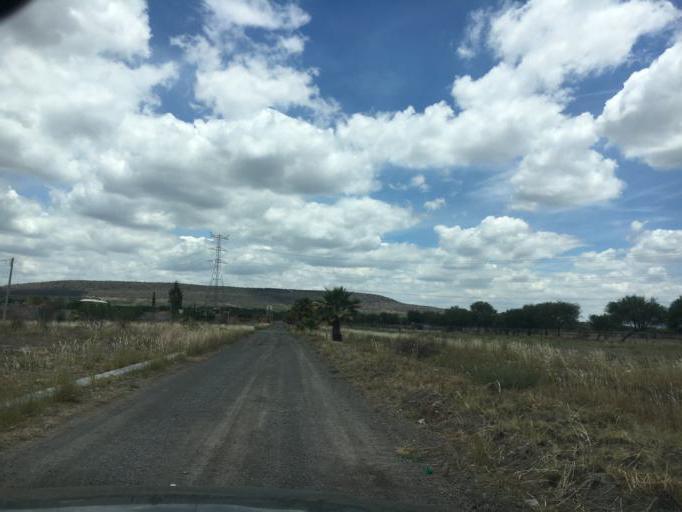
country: MX
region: Guanajuato
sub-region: Leon
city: Plan Guanajuato (La Sandia)
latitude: 20.9240
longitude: -101.7499
